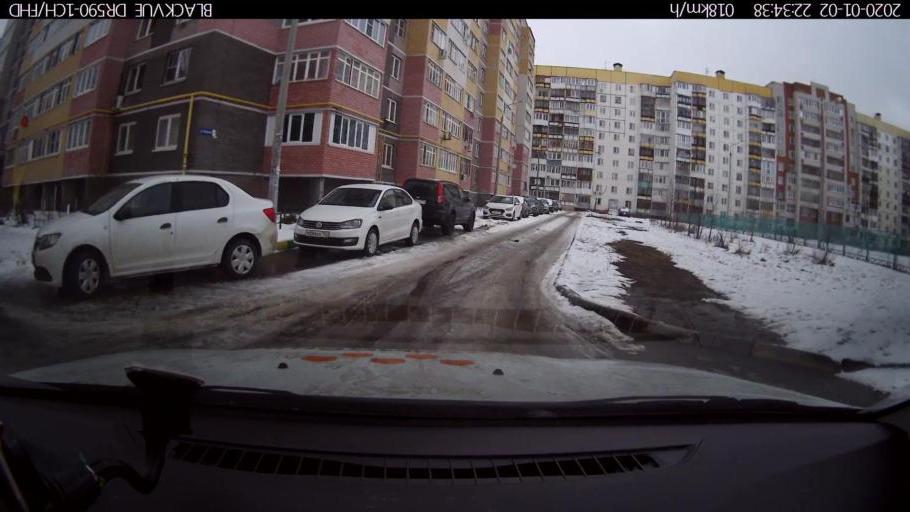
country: RU
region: Nizjnij Novgorod
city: Nizhniy Novgorod
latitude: 56.3372
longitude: 43.9122
